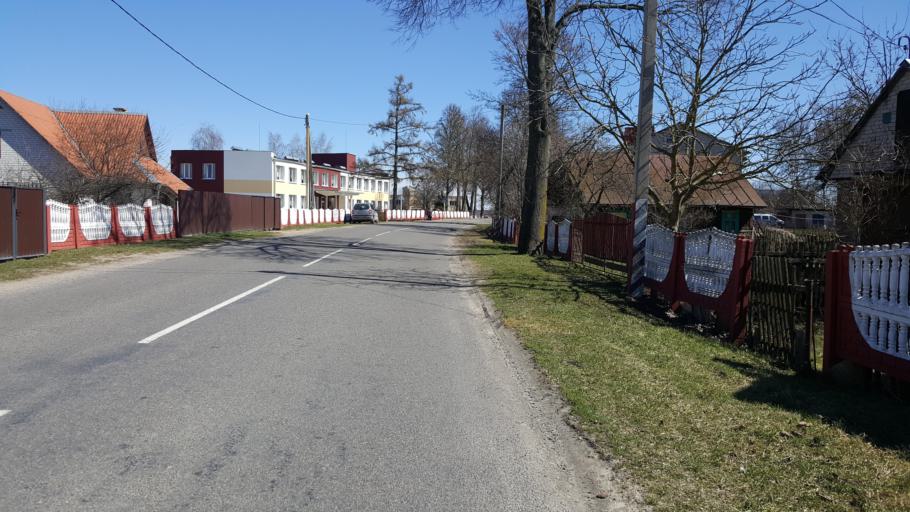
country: BY
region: Brest
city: Zhabinka
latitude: 52.2528
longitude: 23.9055
